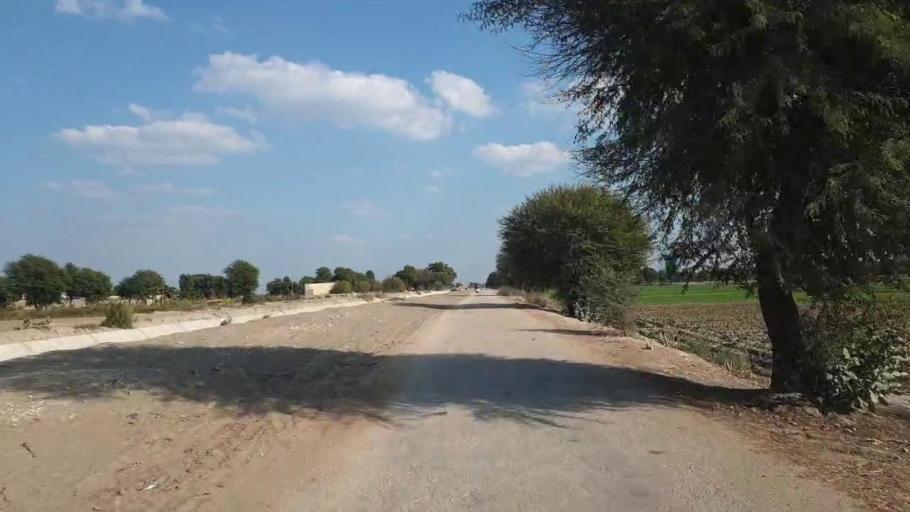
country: PK
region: Sindh
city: Shahpur Chakar
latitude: 26.1036
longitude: 68.5896
